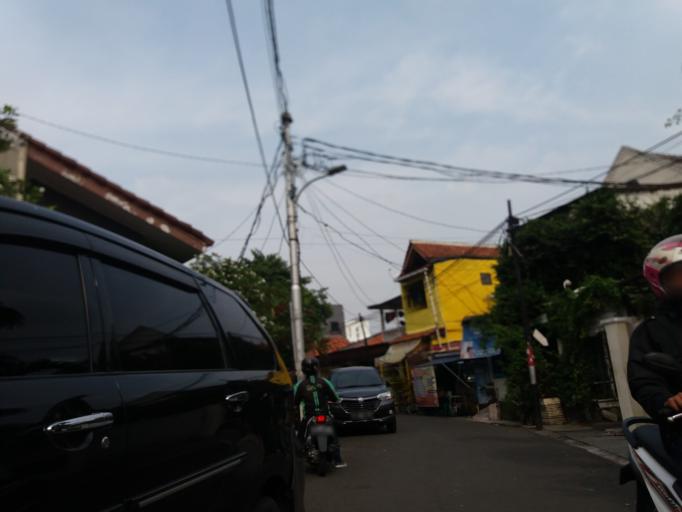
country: ID
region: Jakarta Raya
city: Jakarta
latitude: -6.1846
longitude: 106.8270
